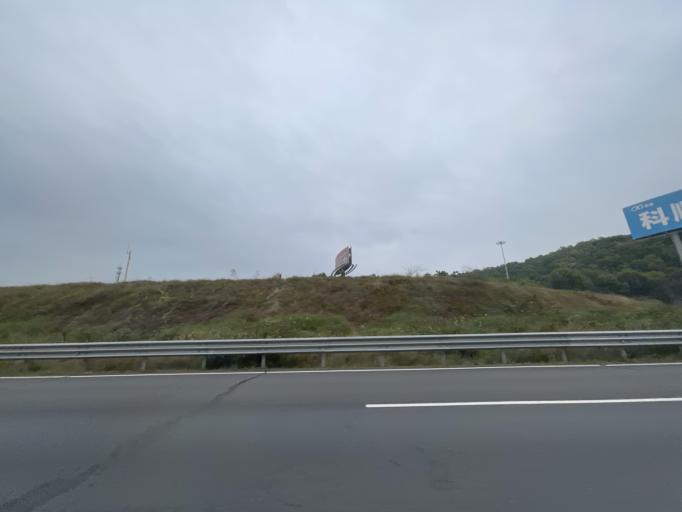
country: CN
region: Guangdong
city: Xinwan
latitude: 22.8076
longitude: 113.6379
